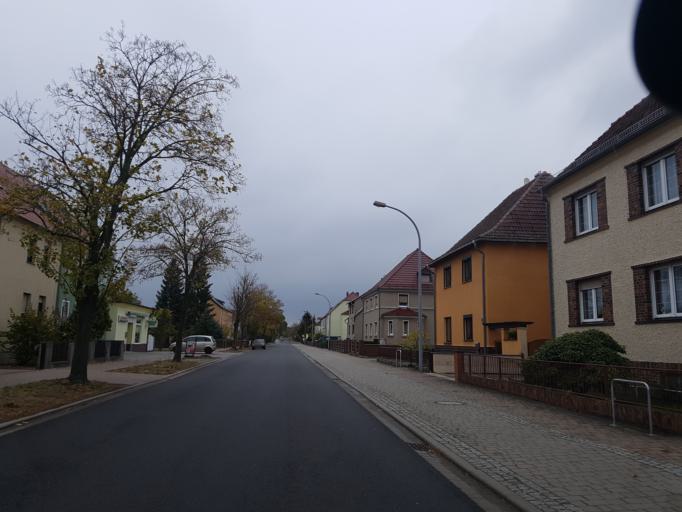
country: DE
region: Brandenburg
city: Falkenberg
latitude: 51.5807
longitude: 13.2329
